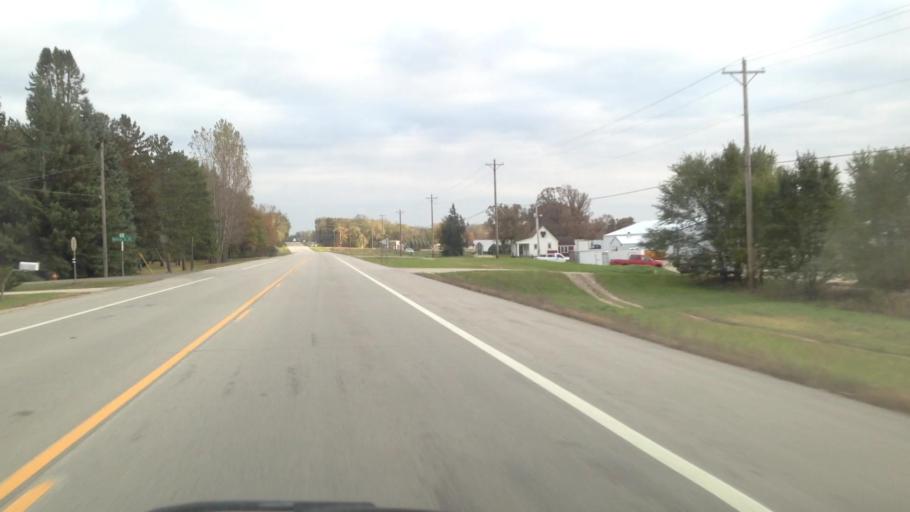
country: US
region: Minnesota
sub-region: Olmsted County
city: Rochester
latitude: 43.9831
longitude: -92.4015
